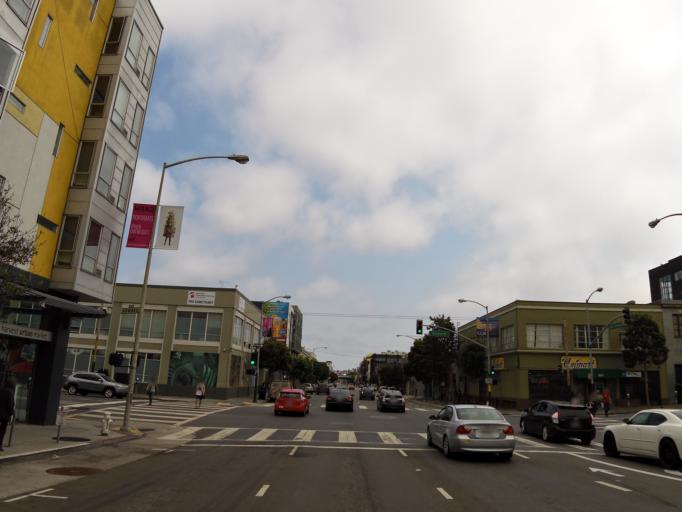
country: US
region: California
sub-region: San Francisco County
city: San Francisco
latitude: 37.7765
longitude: -122.4119
